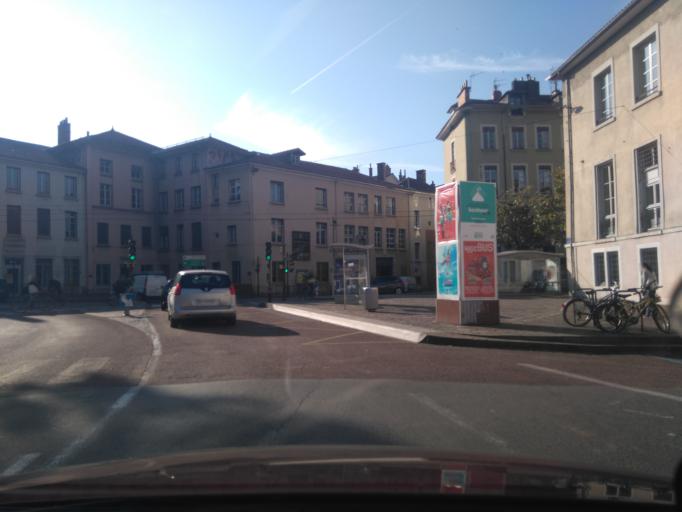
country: FR
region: Rhone-Alpes
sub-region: Departement de l'Isere
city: La Tronche
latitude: 45.1940
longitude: 5.7320
